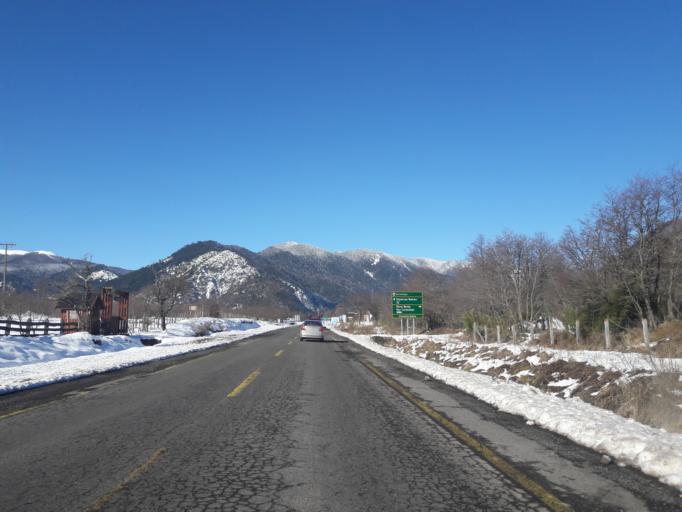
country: CL
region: Araucania
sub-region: Provincia de Cautin
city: Vilcun
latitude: -38.4744
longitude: -71.5532
